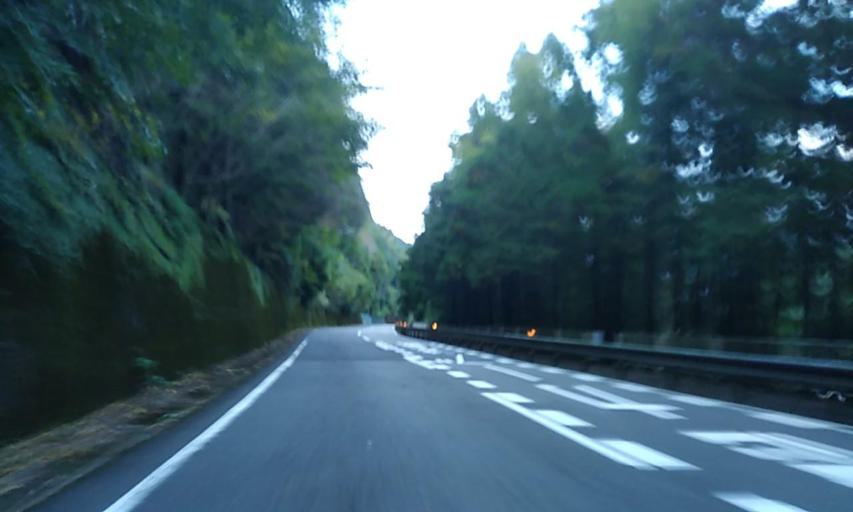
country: JP
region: Wakayama
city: Shingu
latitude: 33.7359
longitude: 135.9402
